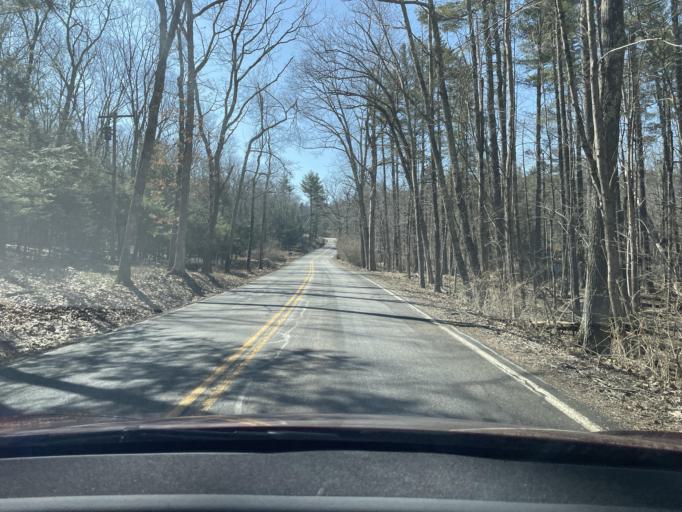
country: US
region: New York
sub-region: Ulster County
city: Woodstock
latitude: 42.0166
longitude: -74.1358
